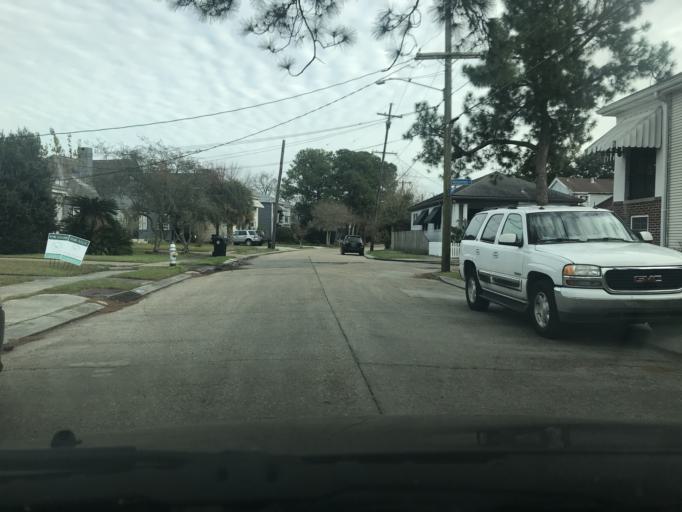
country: US
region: Louisiana
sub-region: Orleans Parish
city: New Orleans
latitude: 29.9567
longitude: -90.1082
